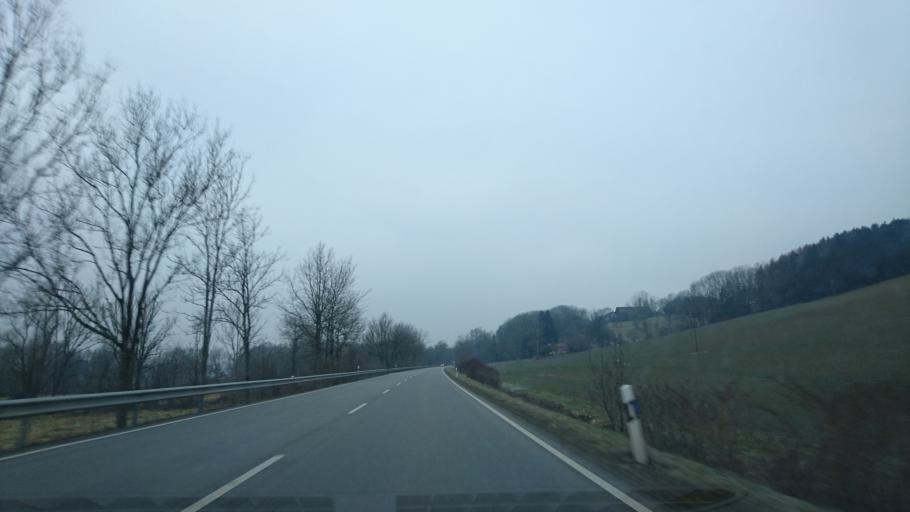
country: DE
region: Bavaria
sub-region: Lower Bavaria
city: Tettenweis
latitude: 48.4188
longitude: 13.2858
